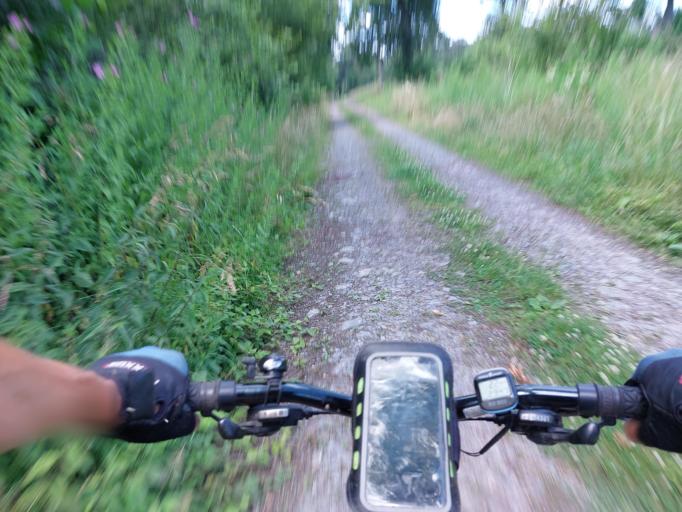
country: BE
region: Wallonia
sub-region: Province du Hainaut
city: Silly
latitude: 50.6090
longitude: 3.9125
